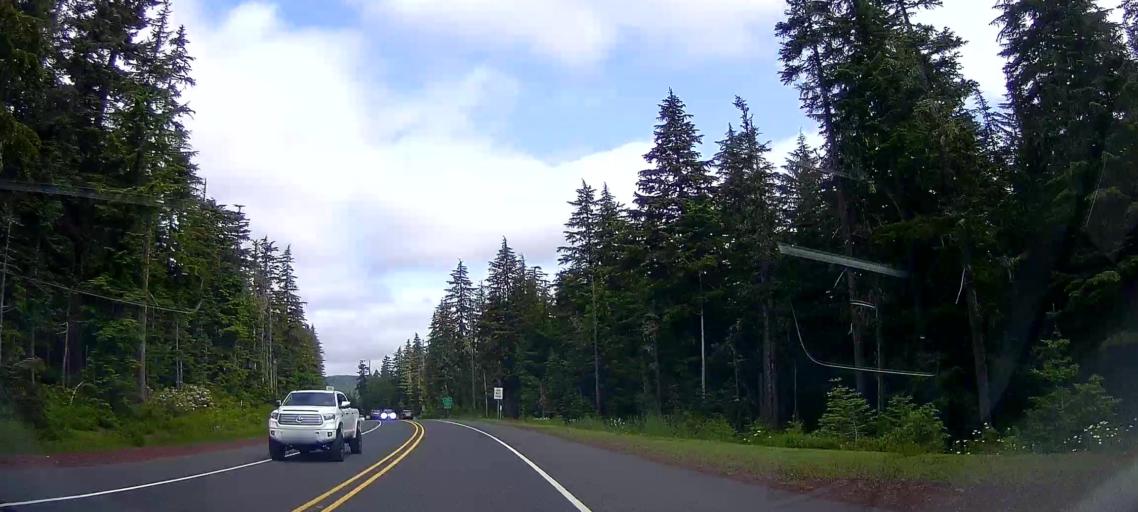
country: US
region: Oregon
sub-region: Clackamas County
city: Mount Hood Village
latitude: 45.2256
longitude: -121.6978
